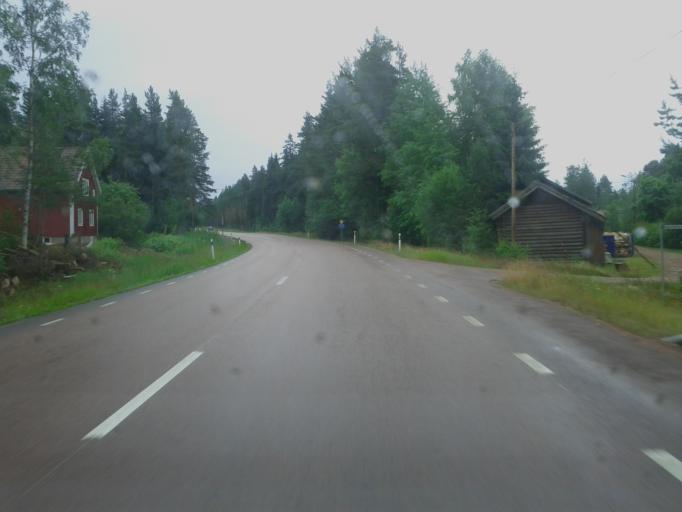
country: SE
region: Dalarna
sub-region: Mora Kommun
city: Mora
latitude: 60.9636
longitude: 14.7085
